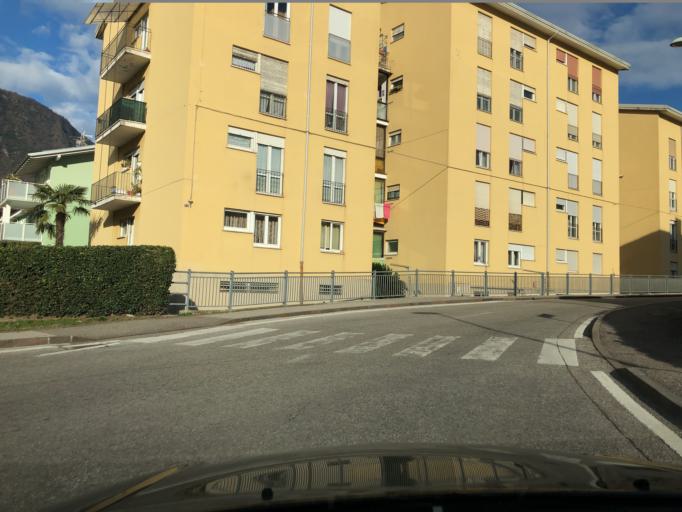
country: IT
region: Trentino-Alto Adige
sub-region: Provincia di Trento
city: Riva del Garda
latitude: 45.8926
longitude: 10.8506
